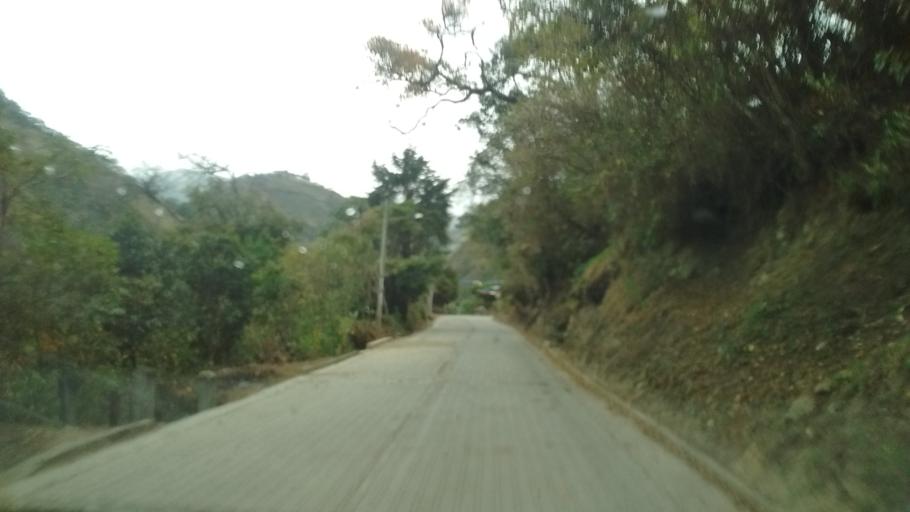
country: CO
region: Cauca
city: La Vega
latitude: 2.0042
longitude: -76.7819
